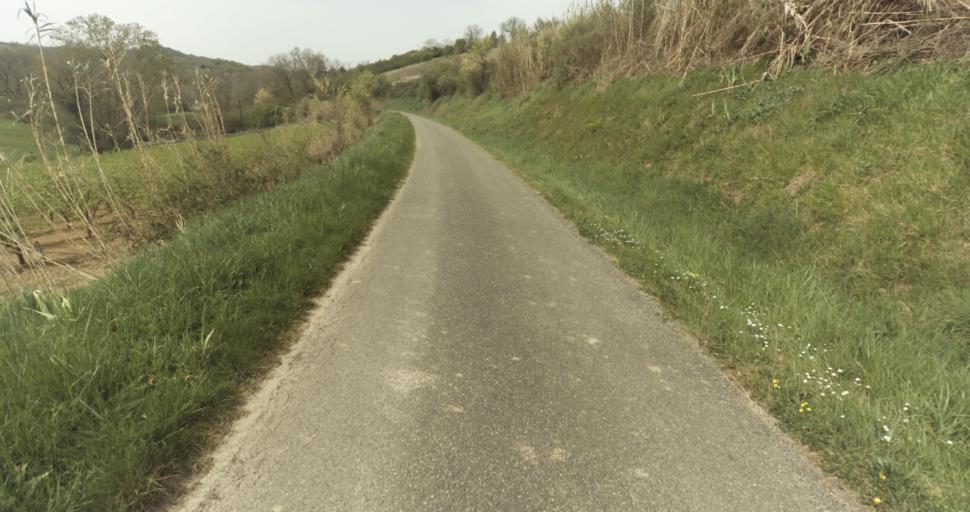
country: FR
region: Midi-Pyrenees
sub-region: Departement du Tarn-et-Garonne
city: Moissac
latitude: 44.1053
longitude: 1.0631
